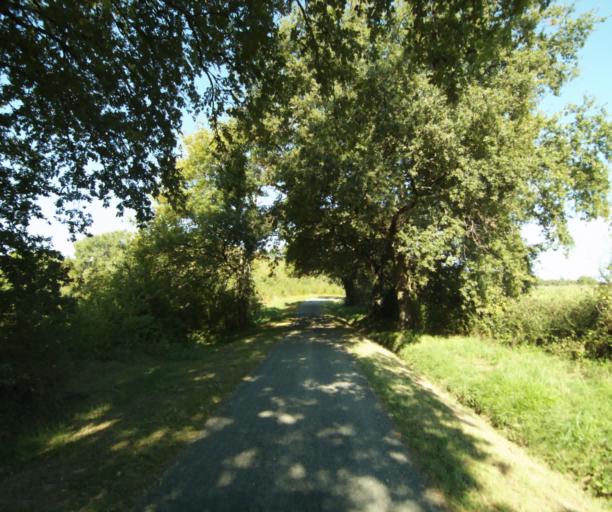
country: FR
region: Midi-Pyrenees
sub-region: Departement du Gers
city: Cazaubon
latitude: 43.9462
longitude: -0.0242
